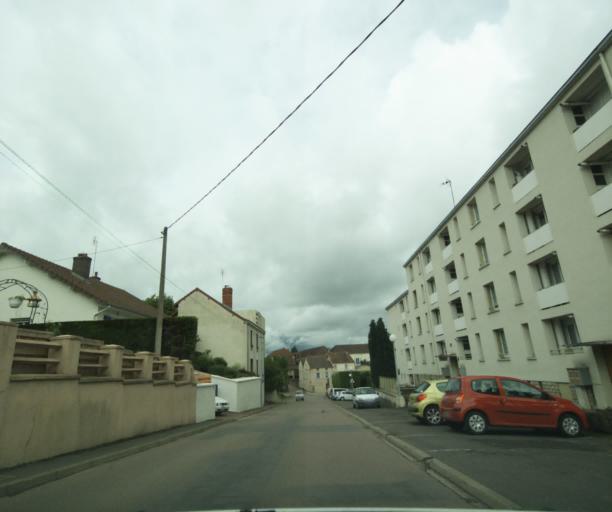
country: FR
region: Bourgogne
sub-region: Departement de Saone-et-Loire
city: Charolles
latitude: 46.4356
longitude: 4.2713
